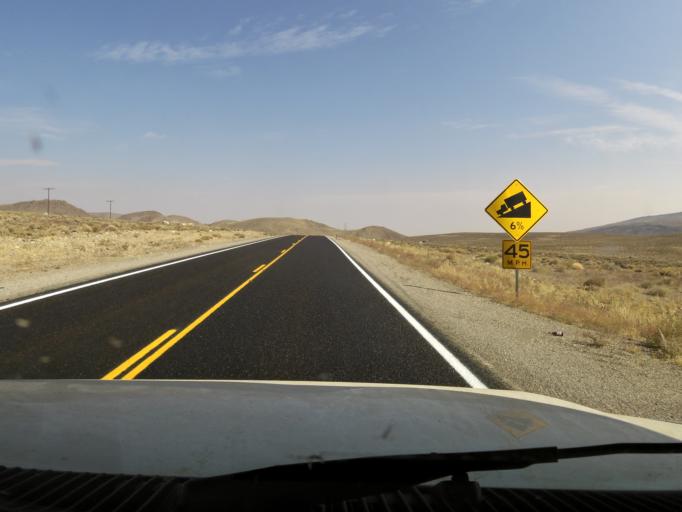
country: US
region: California
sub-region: Inyo County
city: Dixon Lane-Meadow Creek
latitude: 38.0089
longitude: -118.1343
